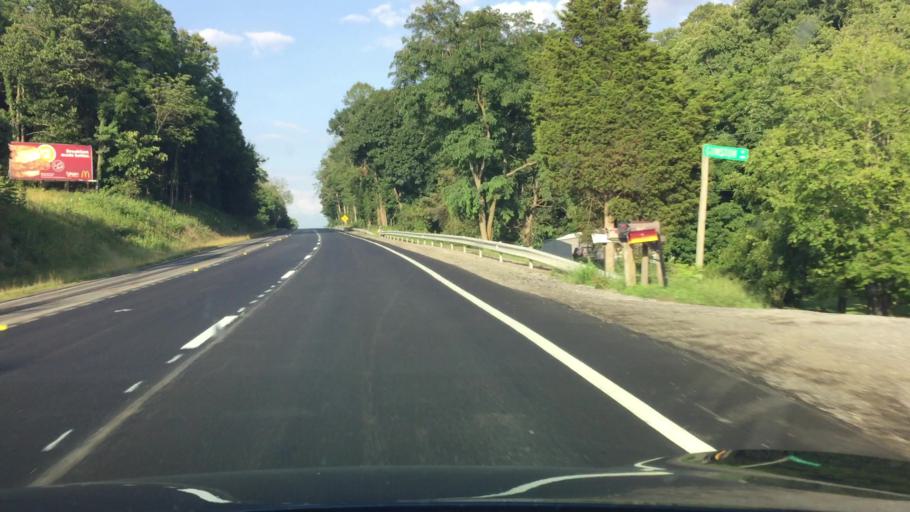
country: US
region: Virginia
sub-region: Montgomery County
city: Christiansburg
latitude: 37.1310
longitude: -80.4766
